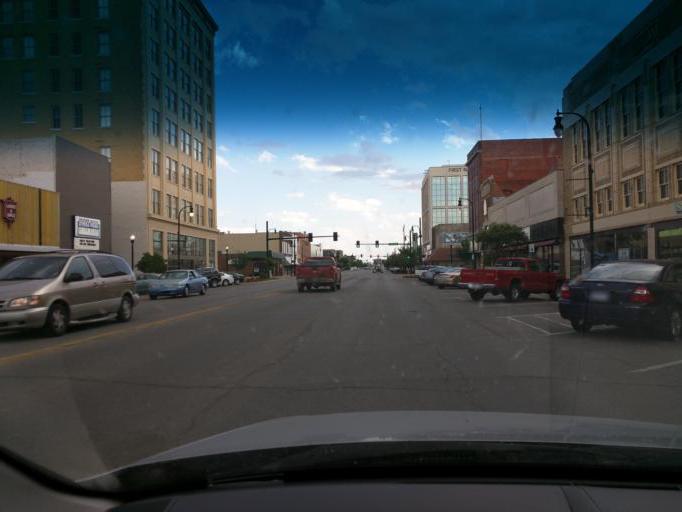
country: US
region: Kansas
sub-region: Reno County
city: Hutchinson
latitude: 38.0544
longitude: -97.9318
